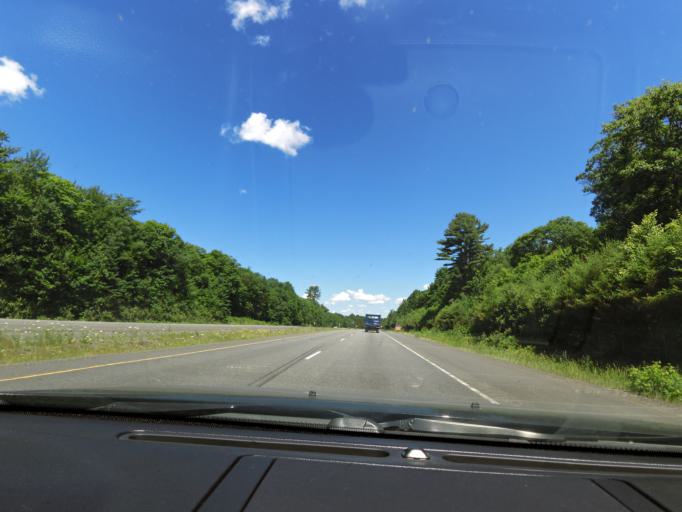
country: CA
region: Ontario
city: Bracebridge
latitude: 45.1009
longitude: -79.3077
